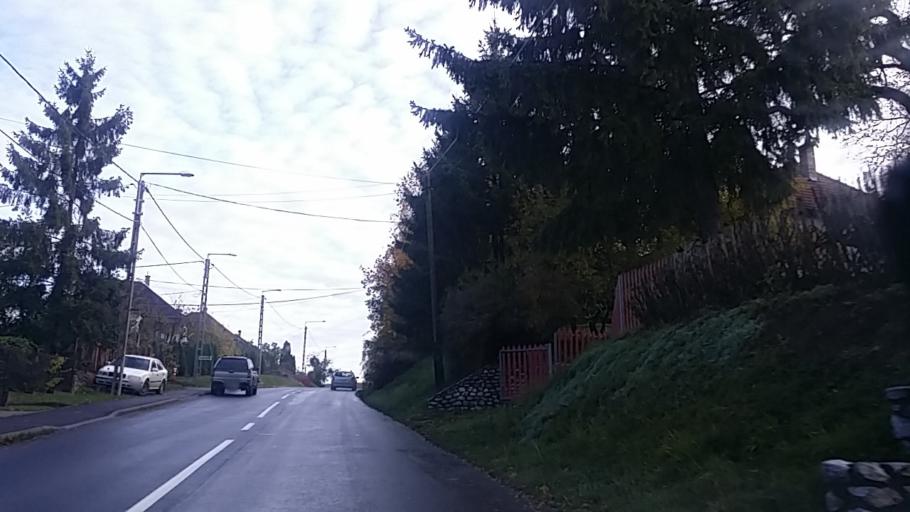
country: HU
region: Heves
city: Szilvasvarad
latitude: 48.1106
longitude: 20.3894
